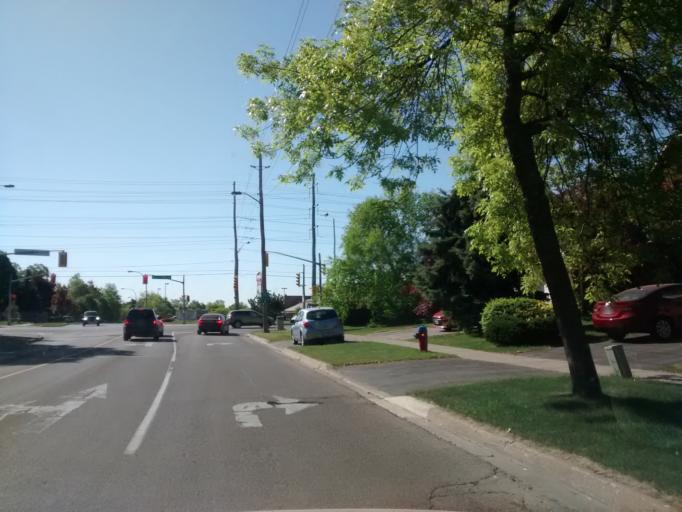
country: CA
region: Ontario
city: Burlington
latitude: 43.3751
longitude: -79.8116
